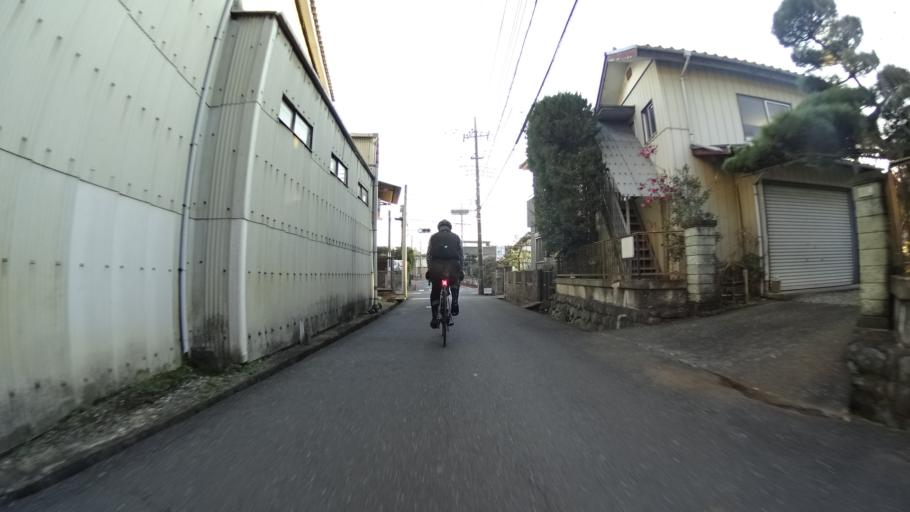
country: JP
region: Saitama
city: Hanno
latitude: 35.8162
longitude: 139.3299
